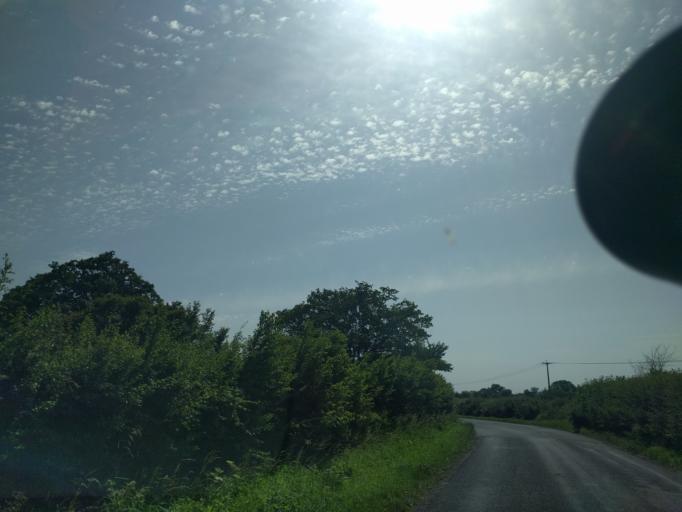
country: GB
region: England
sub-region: Wiltshire
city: Lyneham
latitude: 51.5358
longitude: -1.9784
